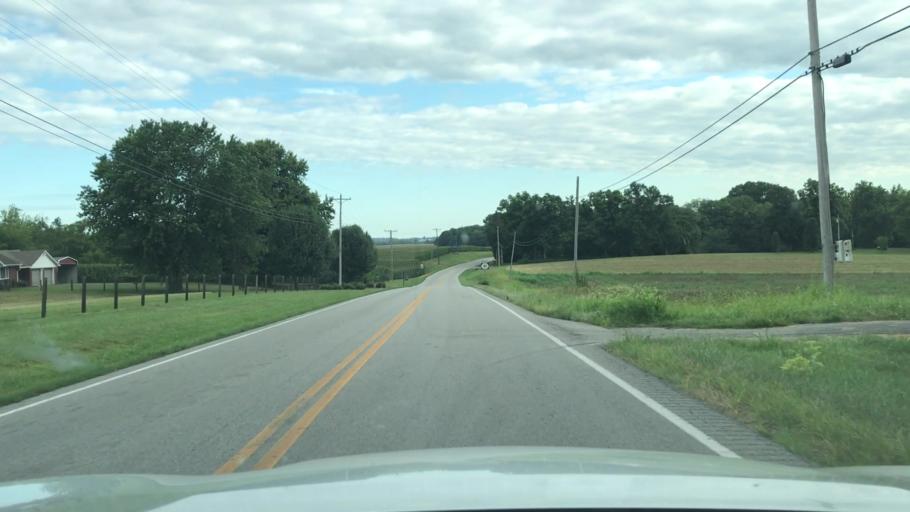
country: US
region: Kentucky
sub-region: Todd County
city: Elkton
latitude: 36.7876
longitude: -87.1640
